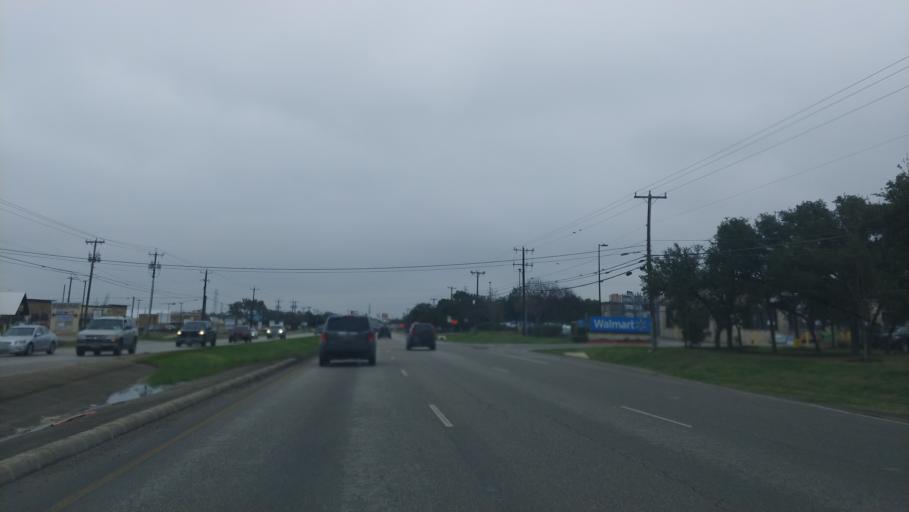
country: US
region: Texas
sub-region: Bexar County
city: Helotes
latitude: 29.5604
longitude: -98.6786
